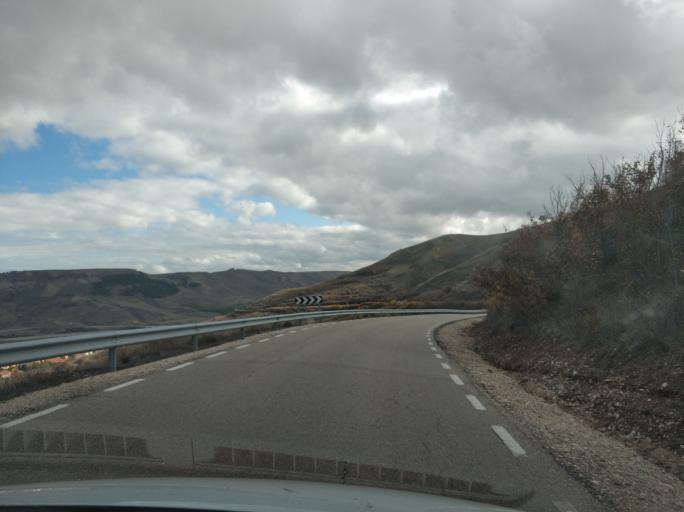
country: ES
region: Castille and Leon
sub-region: Provincia de Soria
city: Medinaceli
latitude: 41.1655
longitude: -2.4338
